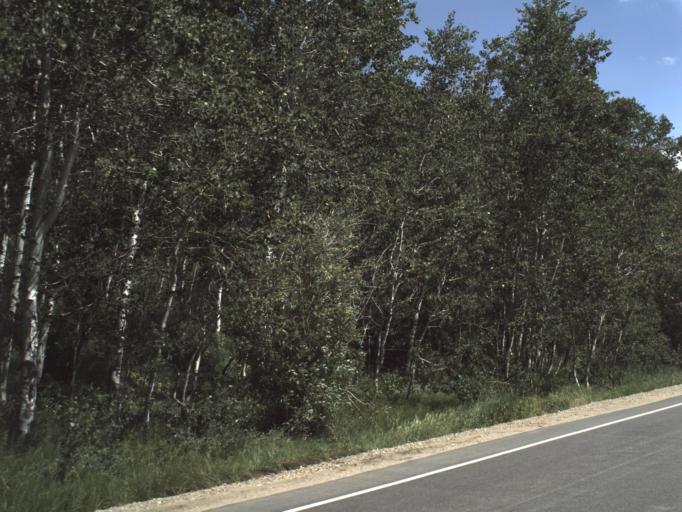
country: US
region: Utah
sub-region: Weber County
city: Wolf Creek
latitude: 41.3939
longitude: -111.5983
